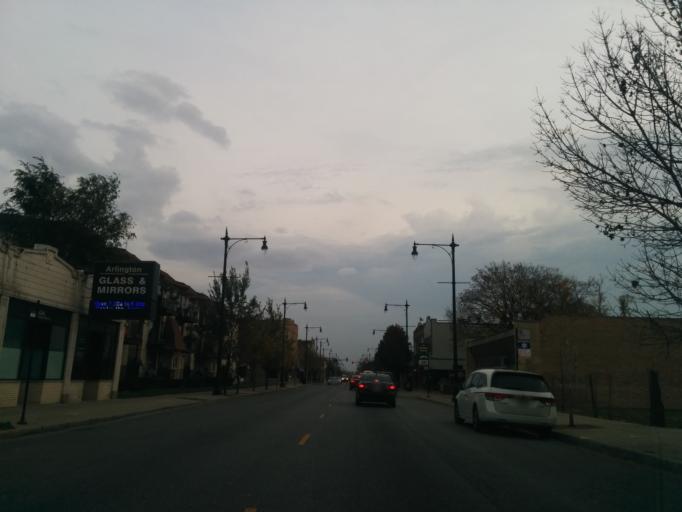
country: US
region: Illinois
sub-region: Cook County
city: Lincolnwood
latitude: 41.9638
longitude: -87.7573
